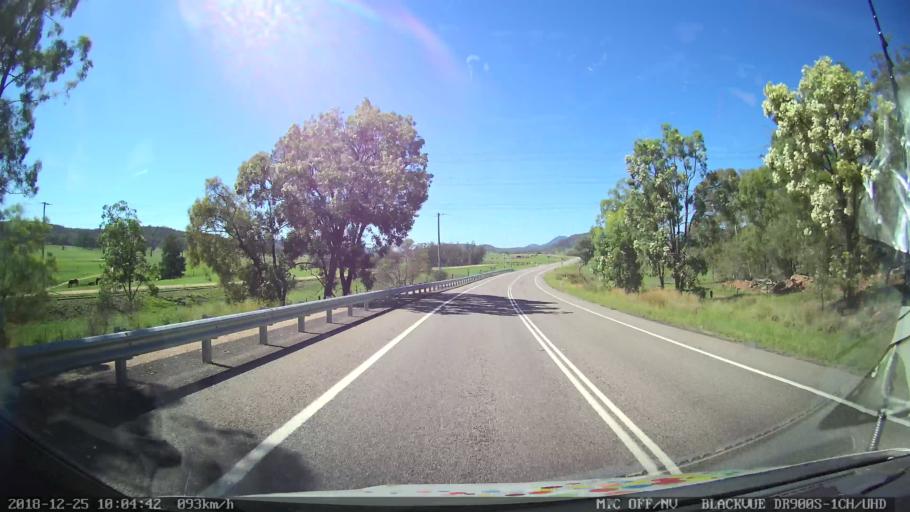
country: AU
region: New South Wales
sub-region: Upper Hunter Shire
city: Merriwa
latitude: -32.2372
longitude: 150.4861
